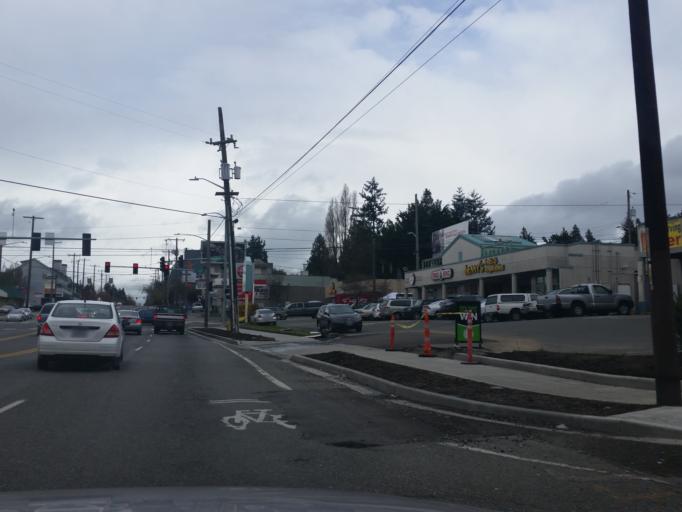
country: US
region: Washington
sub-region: King County
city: Shoreline
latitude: 47.7044
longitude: -122.3554
